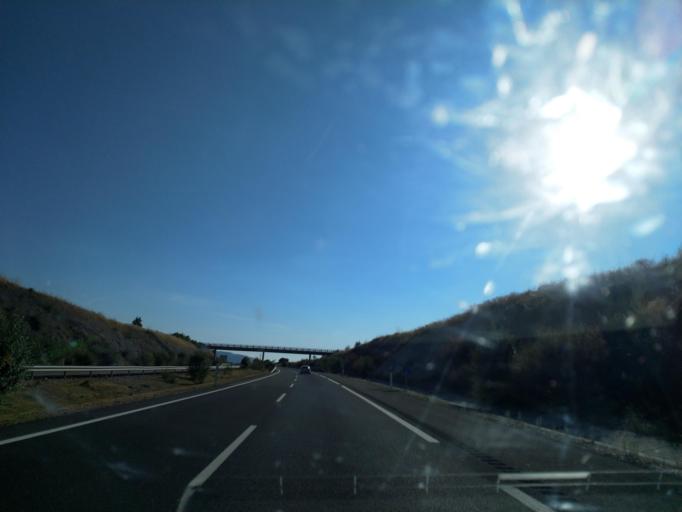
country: ES
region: Castille and Leon
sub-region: Provincia de Segovia
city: Segovia
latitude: 40.8947
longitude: -4.1113
